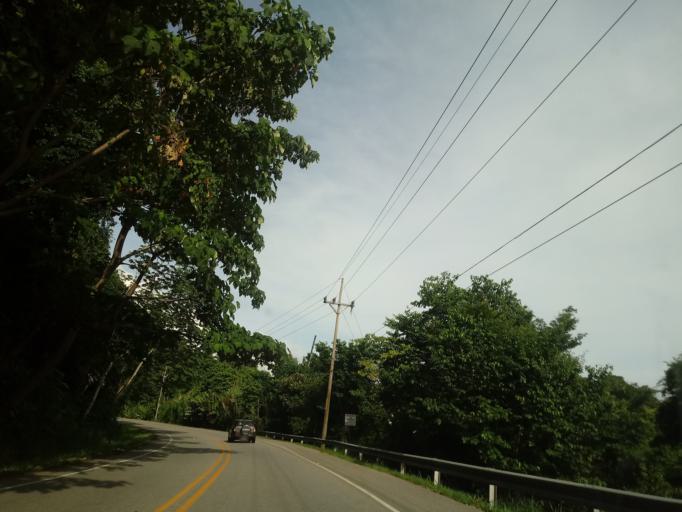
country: CR
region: San Jose
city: Daniel Flores
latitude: 9.1912
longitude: -83.7762
